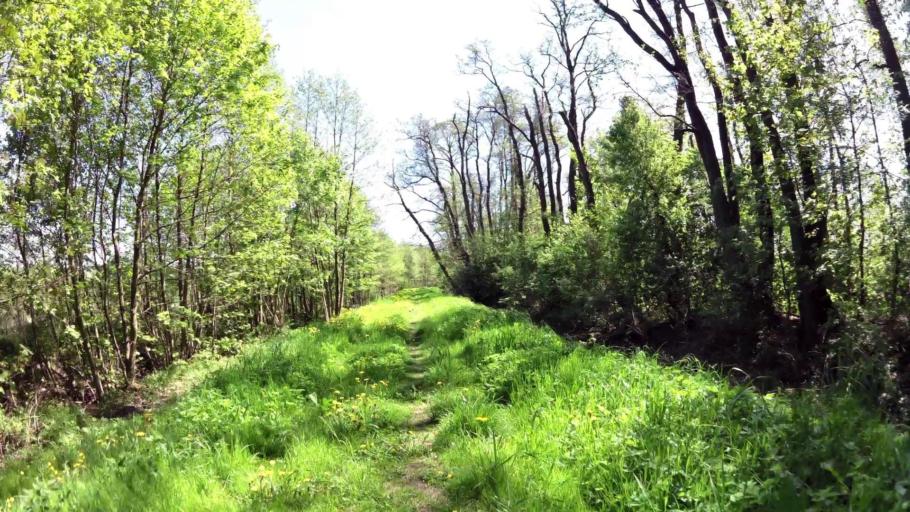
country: PL
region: West Pomeranian Voivodeship
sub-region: Powiat bialogardzki
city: Bialogard
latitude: 54.0000
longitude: 16.0195
